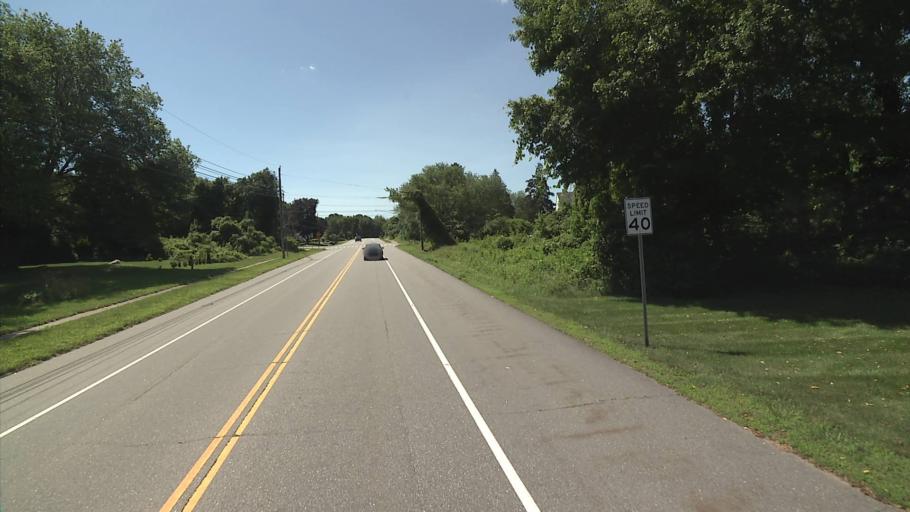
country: US
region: Connecticut
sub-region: New London County
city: Noank
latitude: 41.3318
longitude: -71.9995
